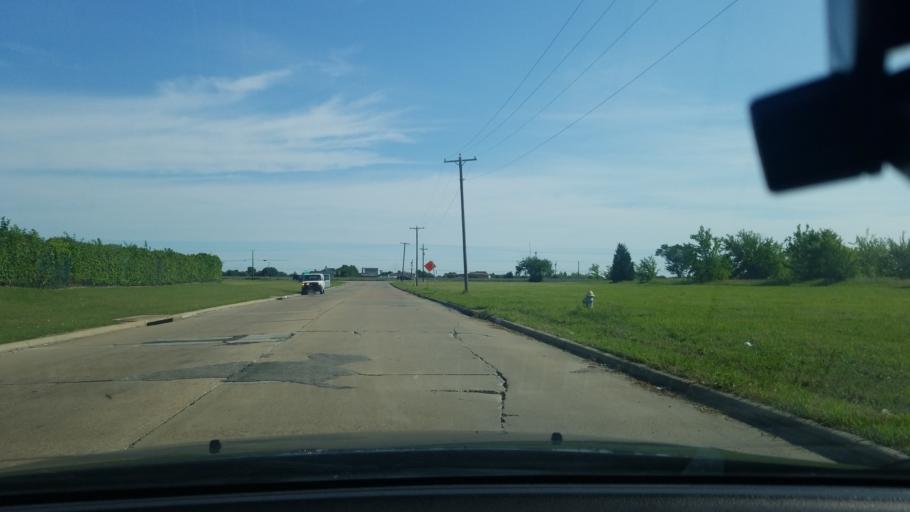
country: US
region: Texas
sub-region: Dallas County
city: Sunnyvale
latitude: 32.7851
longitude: -96.5766
